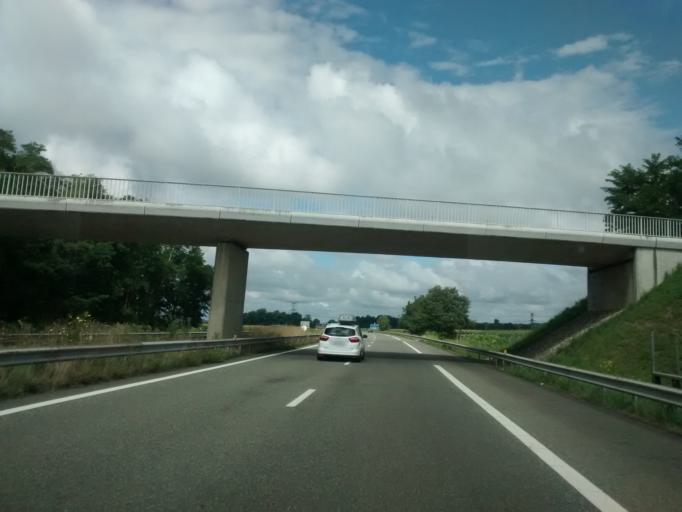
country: FR
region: Aquitaine
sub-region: Departement des Pyrenees-Atlantiques
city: Artix
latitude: 43.4112
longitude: -0.5660
